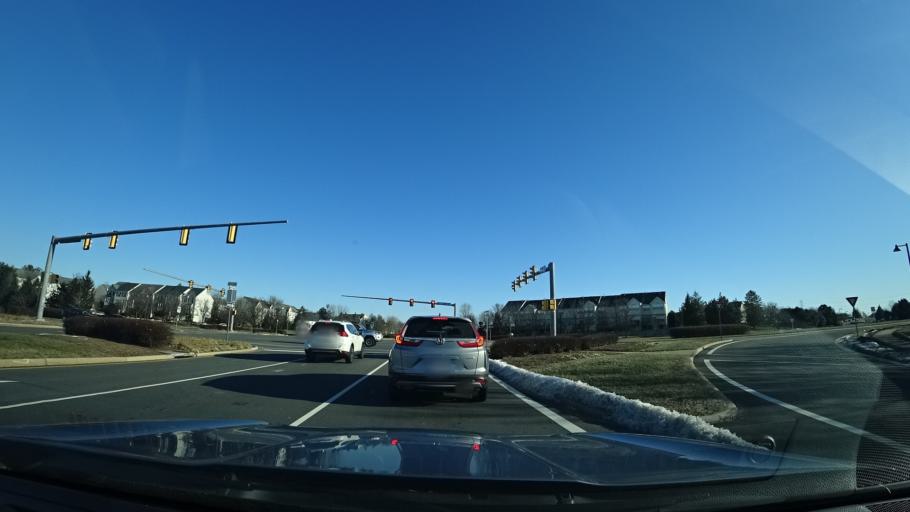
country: US
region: Virginia
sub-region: Loudoun County
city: Ashburn
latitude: 39.0419
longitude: -77.4750
